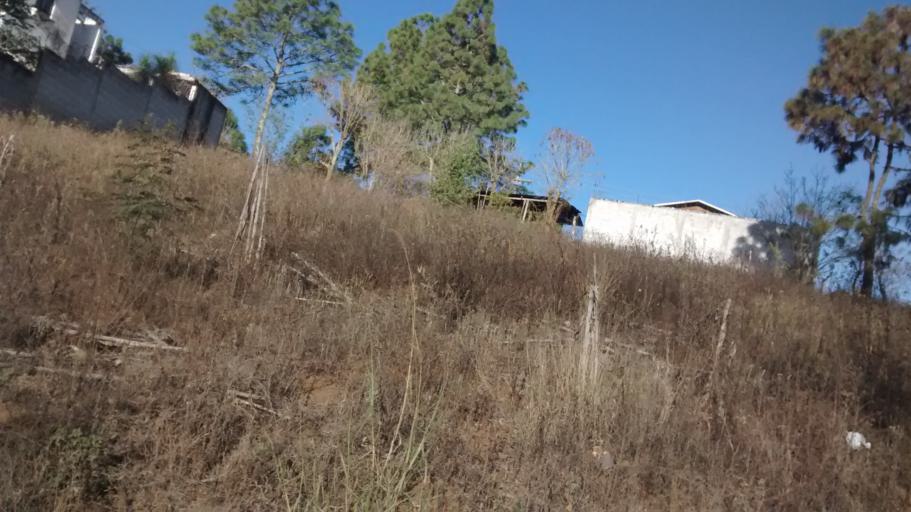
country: GT
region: Sacatepequez
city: Sumpango
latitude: 14.6618
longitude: -90.7165
